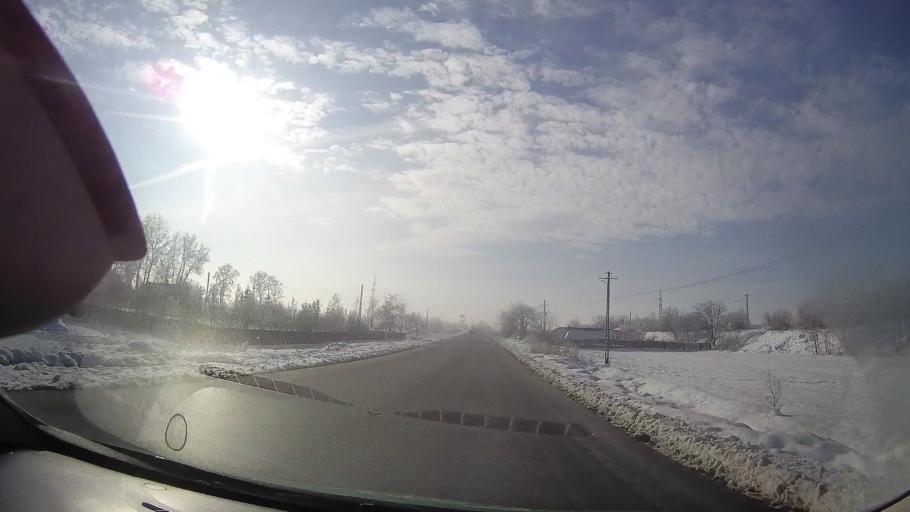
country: RO
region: Neamt
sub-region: Comuna Timisesti
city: Timisesti
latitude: 47.2499
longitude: 26.5485
